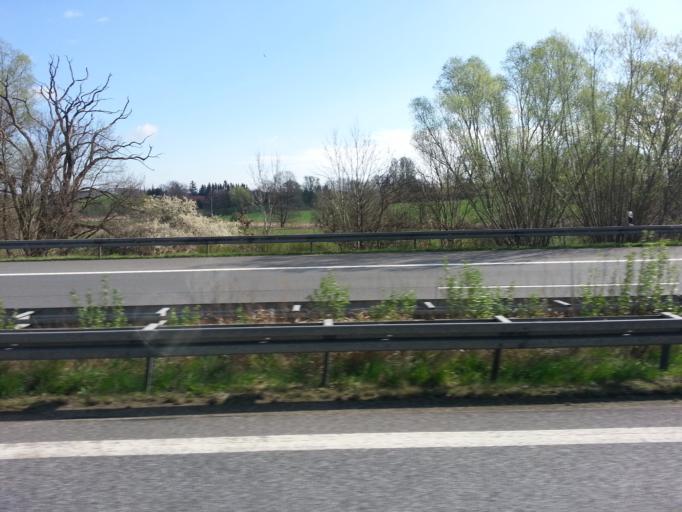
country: DE
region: Mecklenburg-Vorpommern
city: Lalendorf
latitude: 53.6929
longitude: 12.3680
